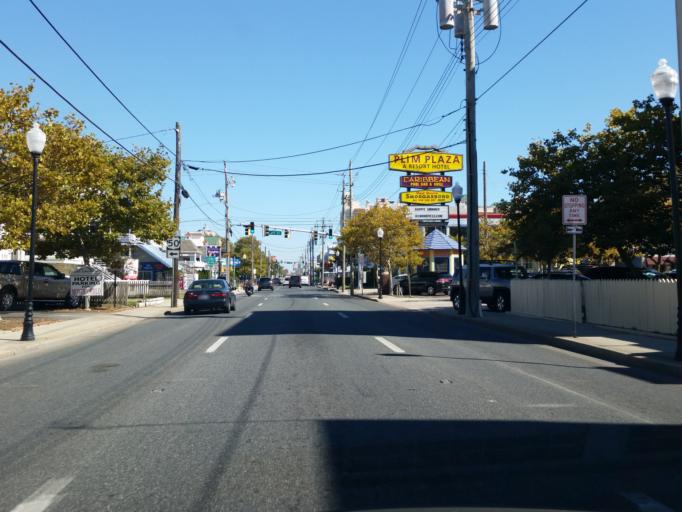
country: US
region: Maryland
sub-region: Worcester County
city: Ocean City
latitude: 38.3330
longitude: -75.0854
